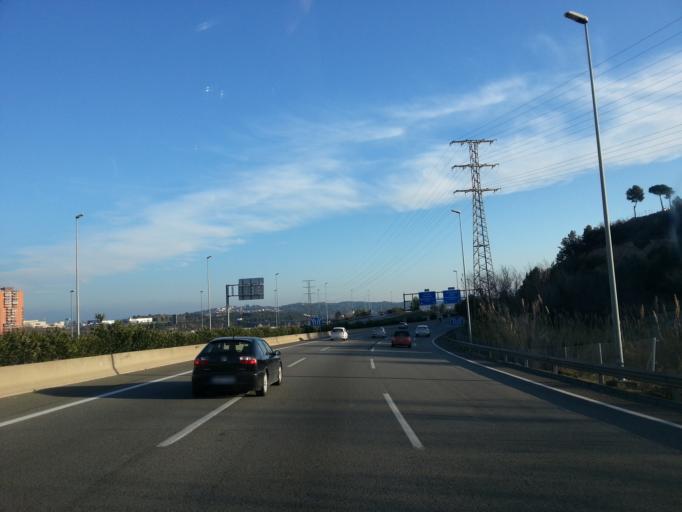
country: ES
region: Catalonia
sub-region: Provincia de Barcelona
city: Terrassa
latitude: 41.5476
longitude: 2.0108
